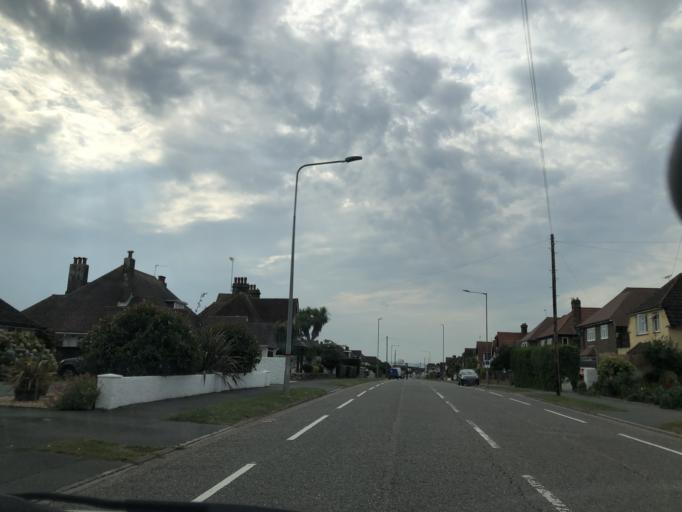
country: GB
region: England
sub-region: East Sussex
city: Bexhill-on-Sea
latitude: 50.8348
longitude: 0.4363
